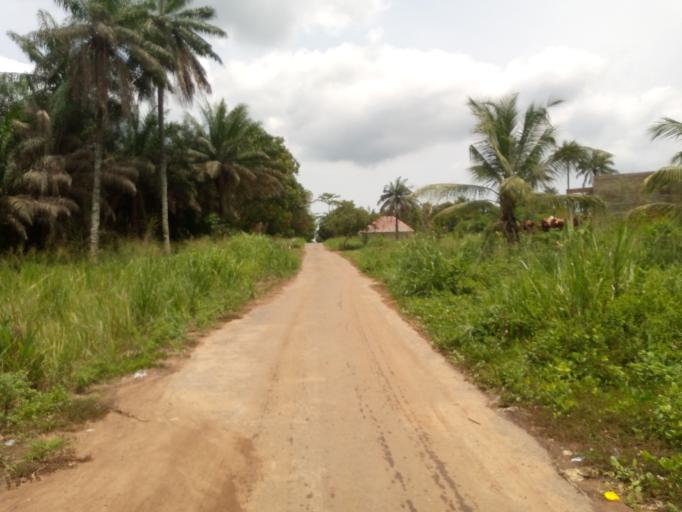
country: SL
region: Western Area
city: Waterloo
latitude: 8.3451
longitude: -12.9847
